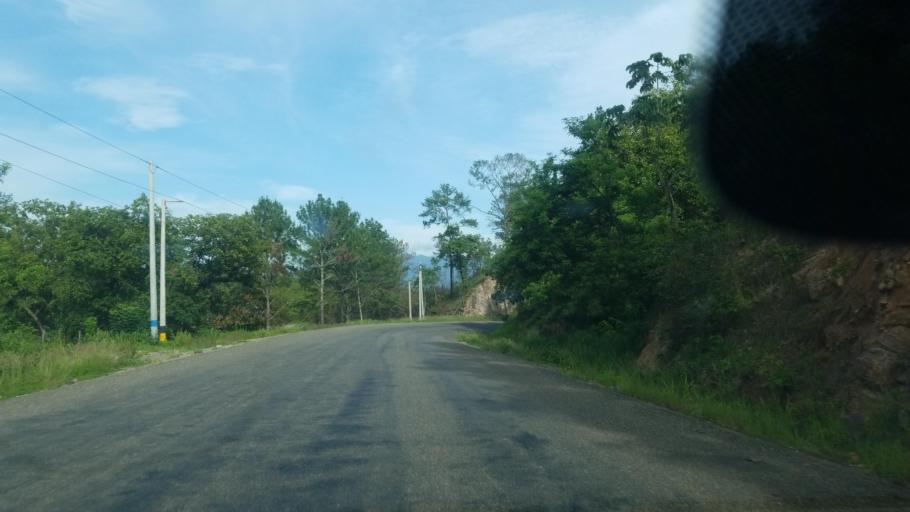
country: HN
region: Santa Barbara
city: Trinidad
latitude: 15.1696
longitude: -88.2600
